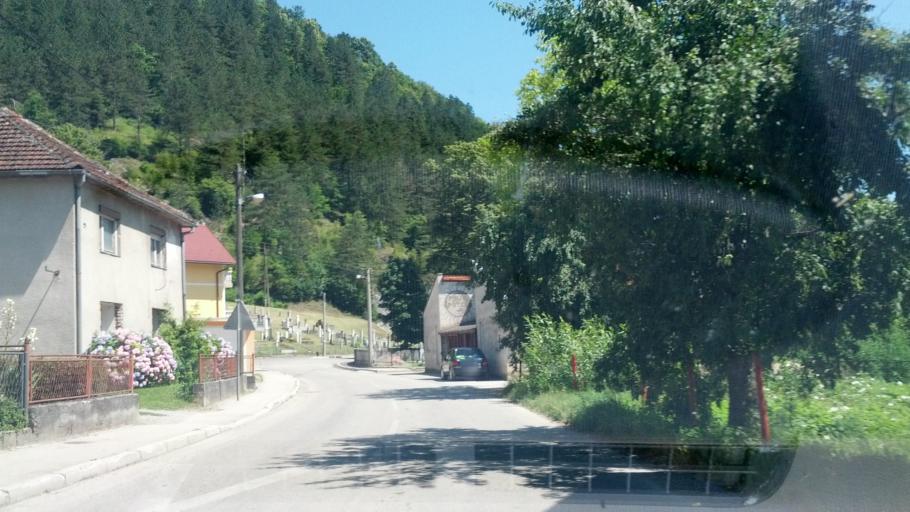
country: BA
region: Federation of Bosnia and Herzegovina
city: Otoka
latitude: 44.9625
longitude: 16.1816
